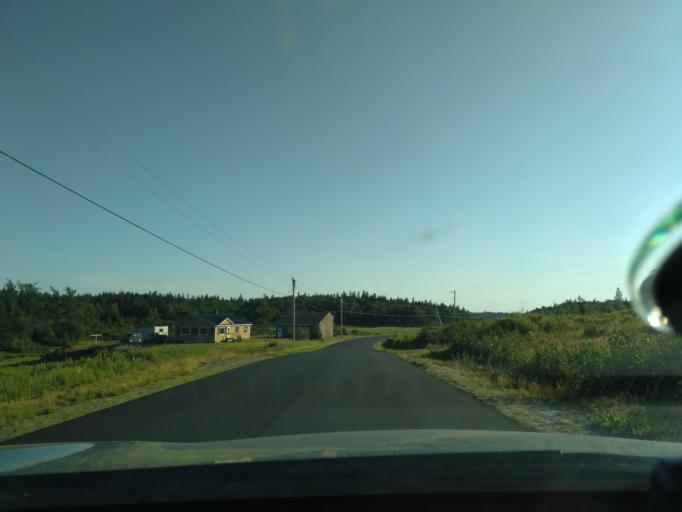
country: US
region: Maine
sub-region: Washington County
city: Machiasport
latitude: 44.6840
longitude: -67.1797
